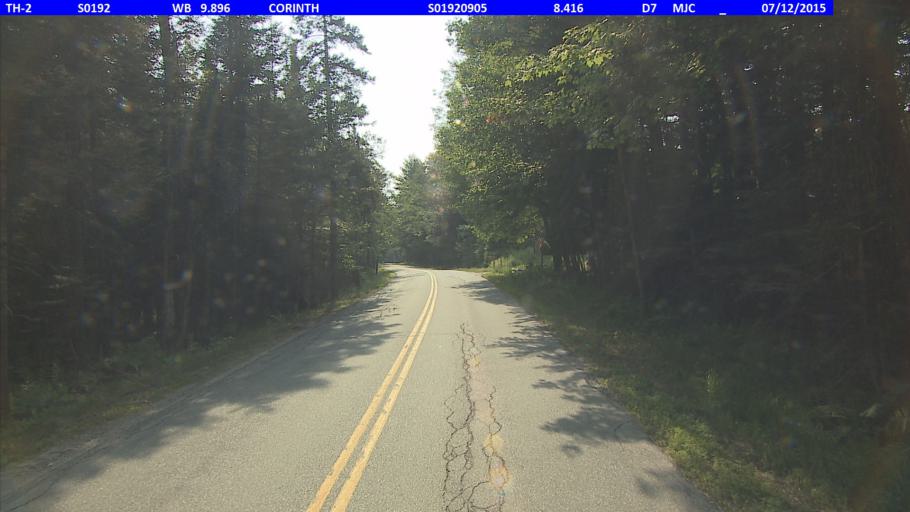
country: US
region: New Hampshire
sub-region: Grafton County
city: Orford
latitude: 44.0217
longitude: -72.2179
